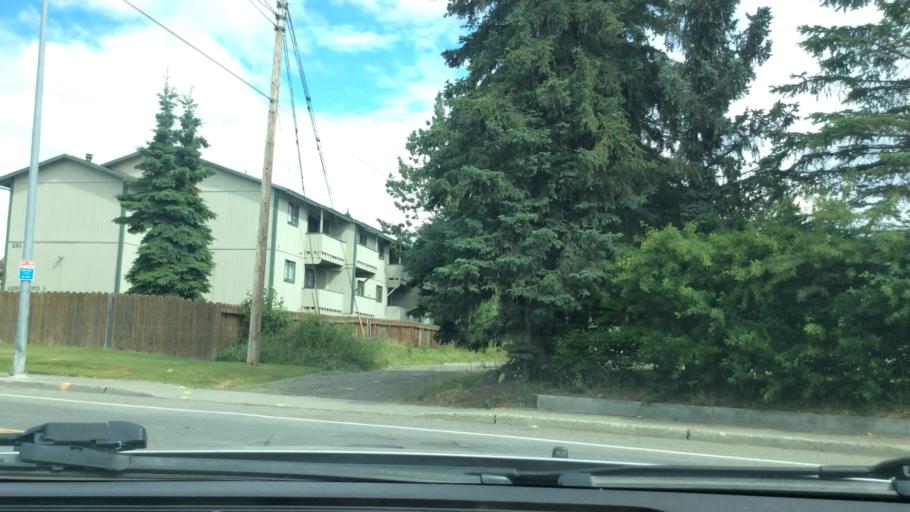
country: US
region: Alaska
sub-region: Anchorage Municipality
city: Anchorage
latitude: 61.2205
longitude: -149.7933
